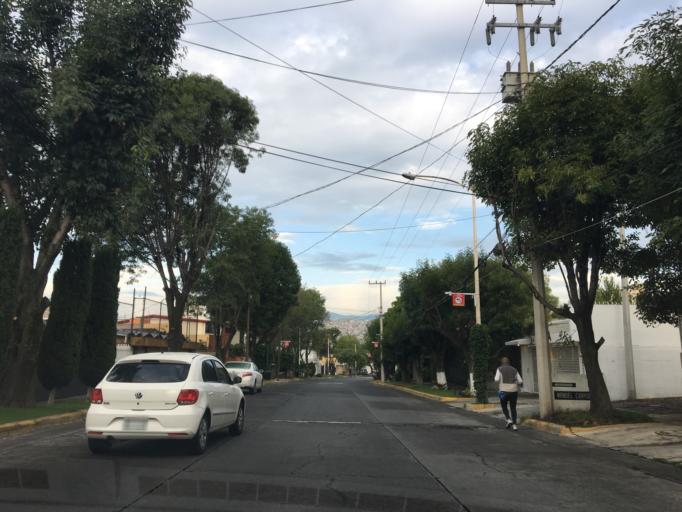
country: MX
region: Mexico
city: Naucalpan de Juarez
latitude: 19.4991
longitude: -99.2457
